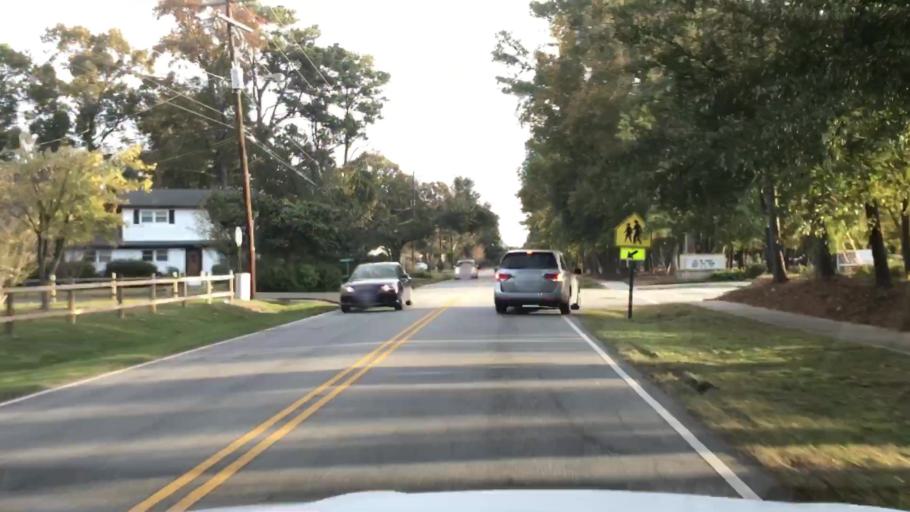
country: US
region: South Carolina
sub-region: Charleston County
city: North Charleston
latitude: 32.8129
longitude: -80.0191
